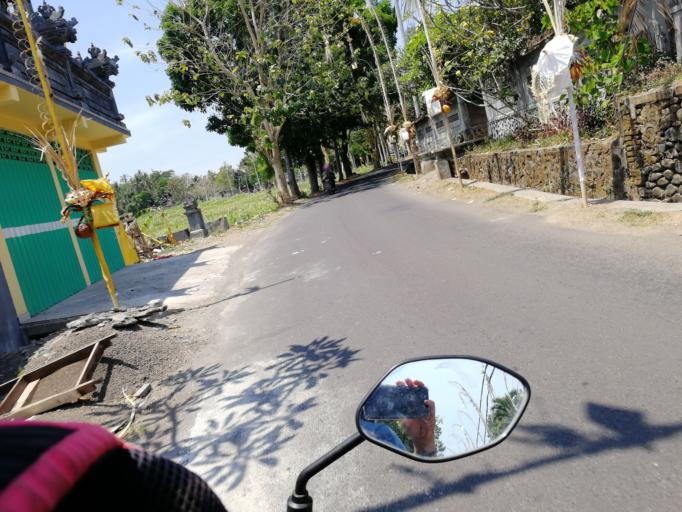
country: ID
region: Bali
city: Banjar Timbrah
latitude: -8.4697
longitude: 115.5917
